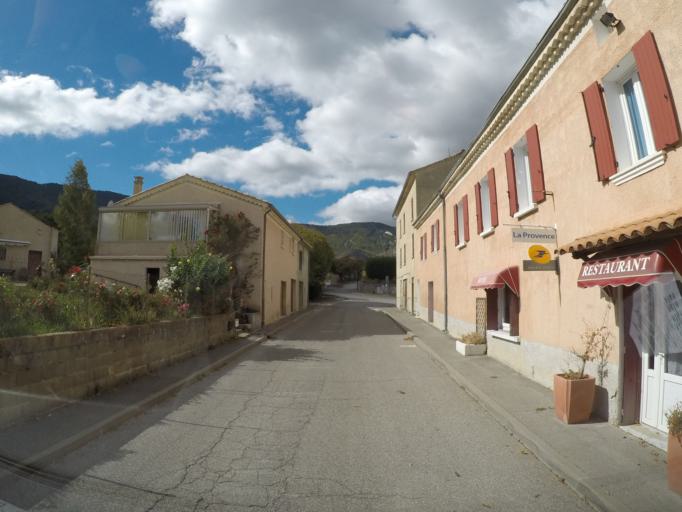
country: FR
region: Provence-Alpes-Cote d'Azur
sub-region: Departement du Vaucluse
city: Sault
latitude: 44.1721
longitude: 5.6086
